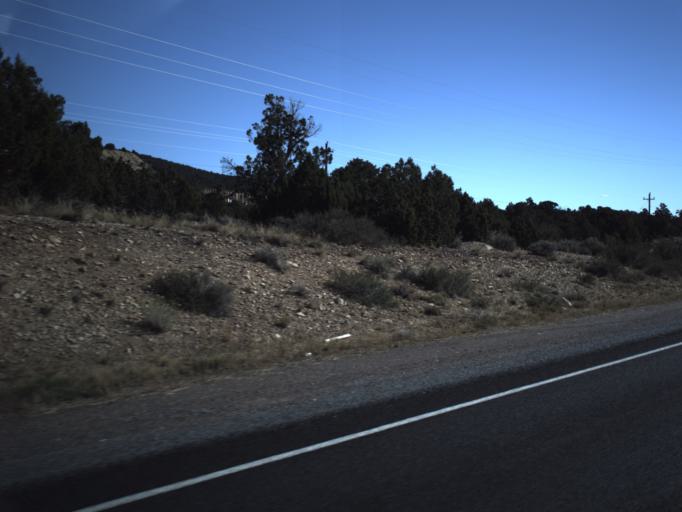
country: US
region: Utah
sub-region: Iron County
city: Cedar City
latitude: 37.6112
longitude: -113.3836
